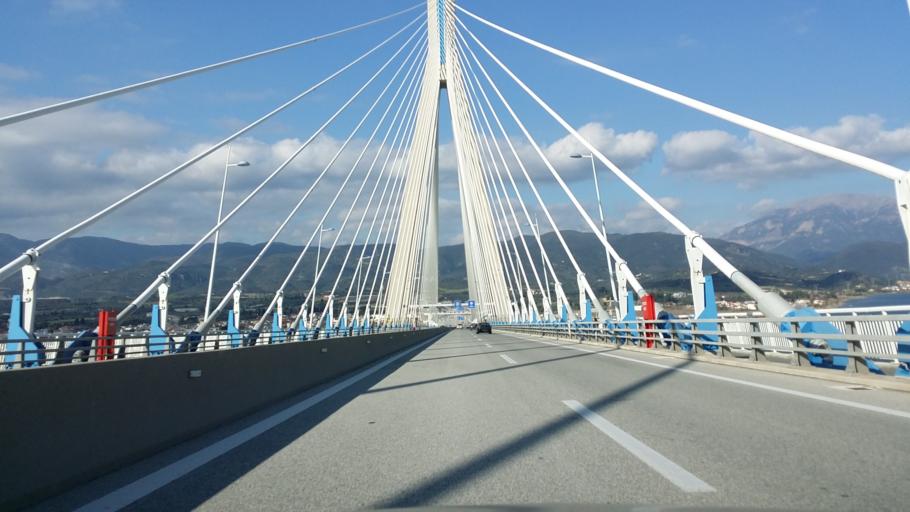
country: GR
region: West Greece
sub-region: Nomos Aitolias kai Akarnanias
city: Antirrio
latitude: 38.3251
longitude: 21.7707
